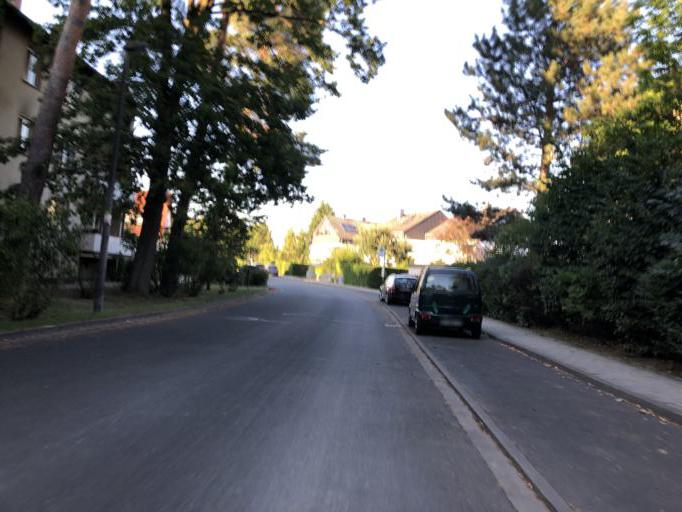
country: DE
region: Bavaria
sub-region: Regierungsbezirk Mittelfranken
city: Buckenhof
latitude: 49.5891
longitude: 11.0487
